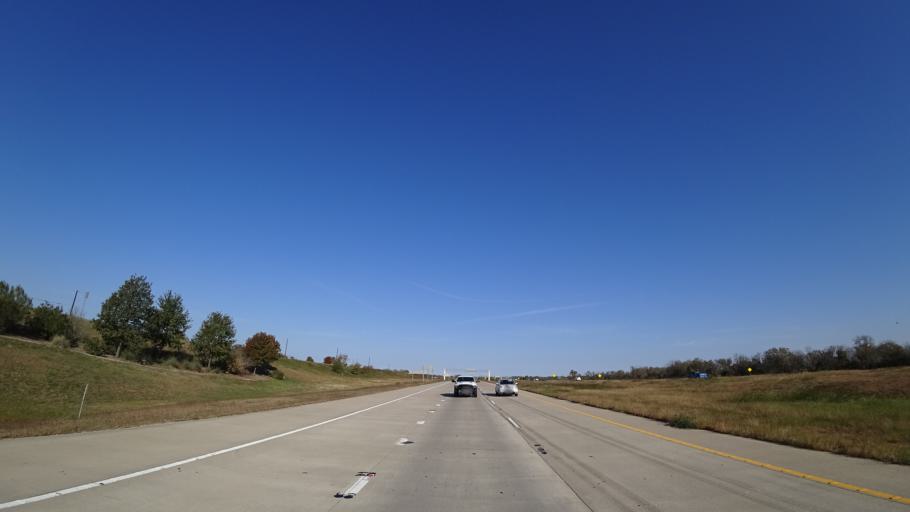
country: US
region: Texas
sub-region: Travis County
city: Pflugerville
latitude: 30.4247
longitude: -97.5886
